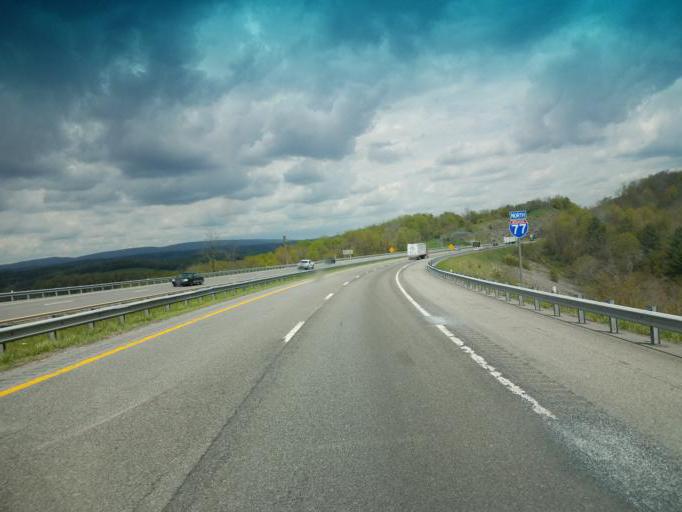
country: US
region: Virginia
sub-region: Bland County
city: Bland
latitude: 37.0461
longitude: -81.1392
